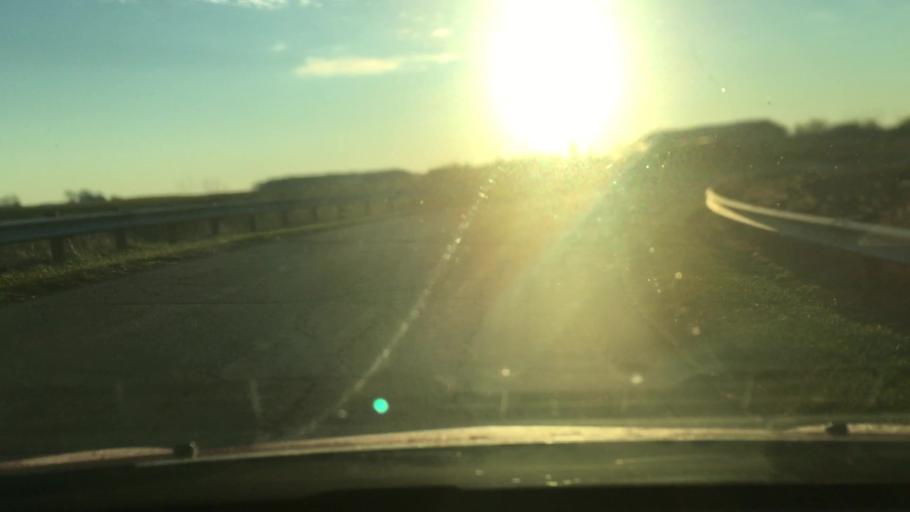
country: US
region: Ohio
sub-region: Wayne County
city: Wooster
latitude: 40.7757
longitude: -81.9118
